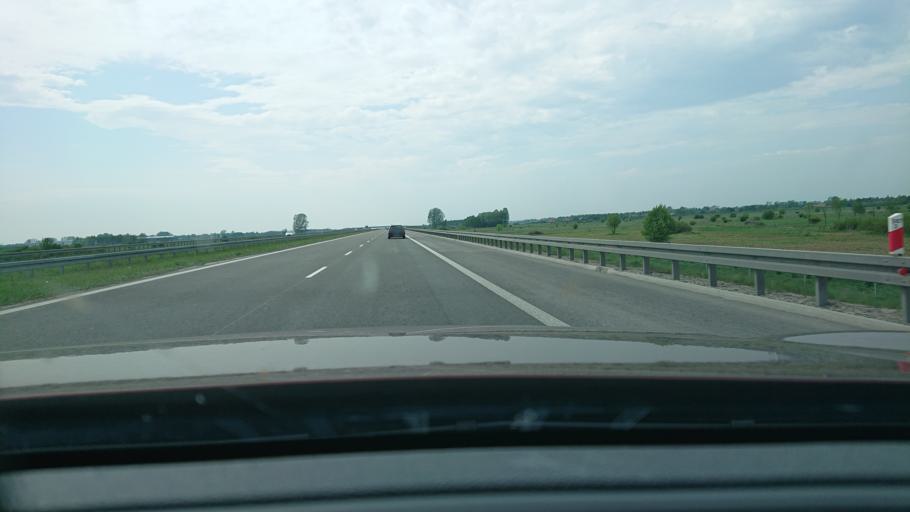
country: PL
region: Subcarpathian Voivodeship
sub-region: Powiat rzeszowski
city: Wolka Podlesna
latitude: 50.0940
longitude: 22.1375
